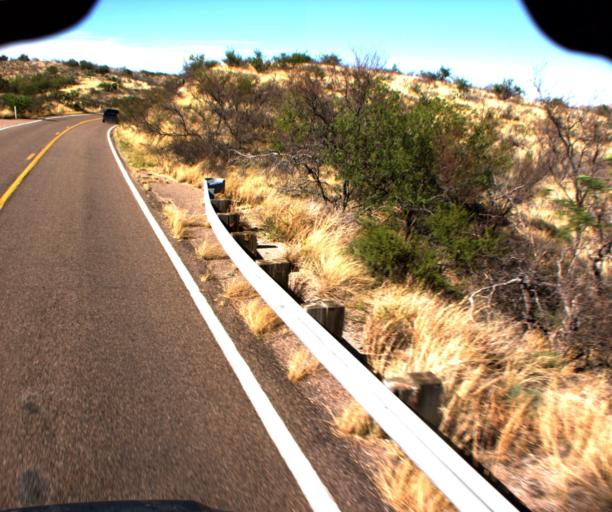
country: US
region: Arizona
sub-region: Pima County
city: Corona de Tucson
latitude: 31.8398
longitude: -110.7017
